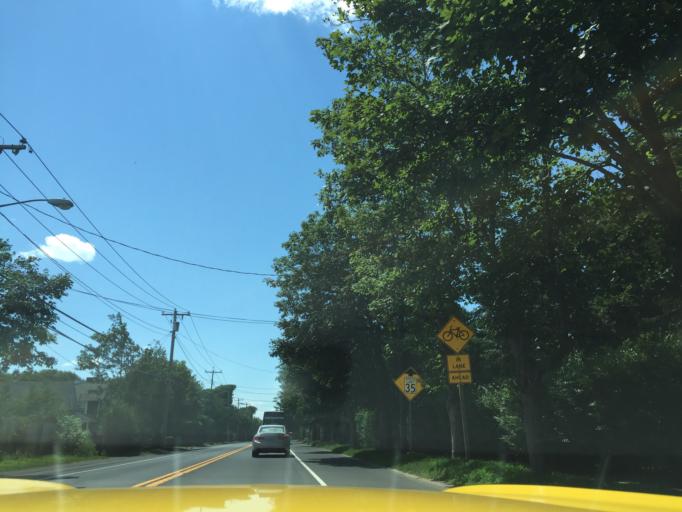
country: US
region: New York
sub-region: Suffolk County
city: Amagansett
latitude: 40.9782
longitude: -72.1156
